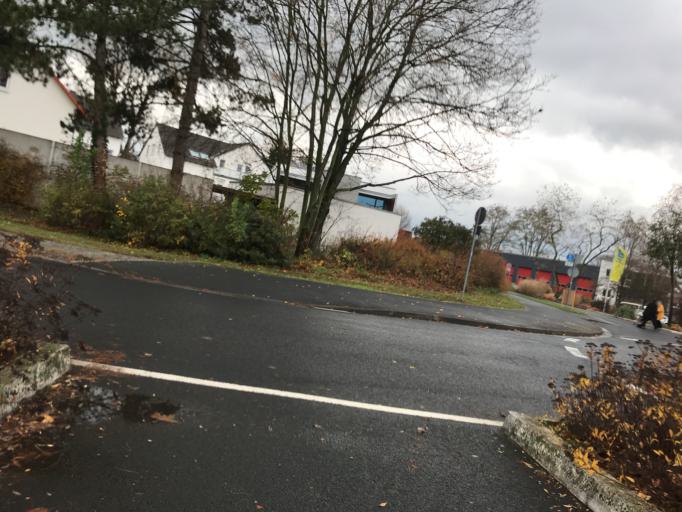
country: DE
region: Rheinland-Pfalz
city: Bodenheim
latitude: 49.9529
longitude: 8.3101
